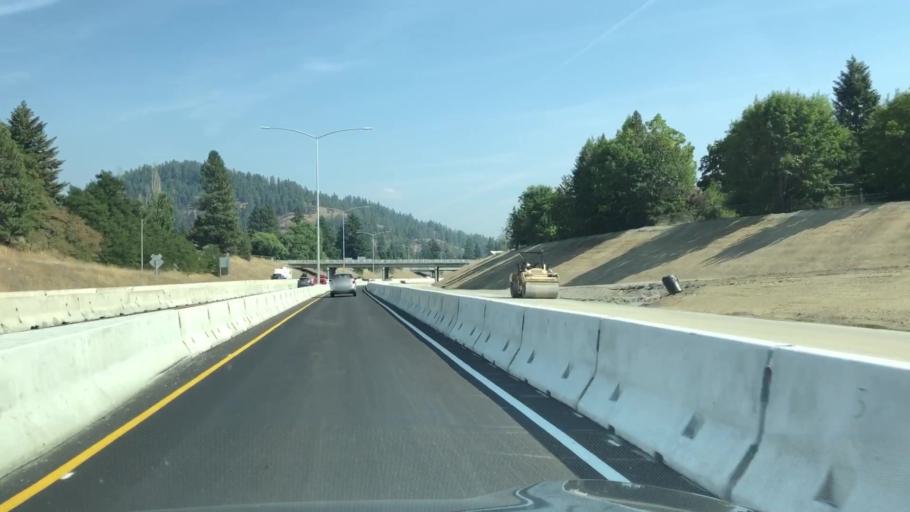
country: US
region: Idaho
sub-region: Kootenai County
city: Coeur d'Alene
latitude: 47.6973
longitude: -116.7794
